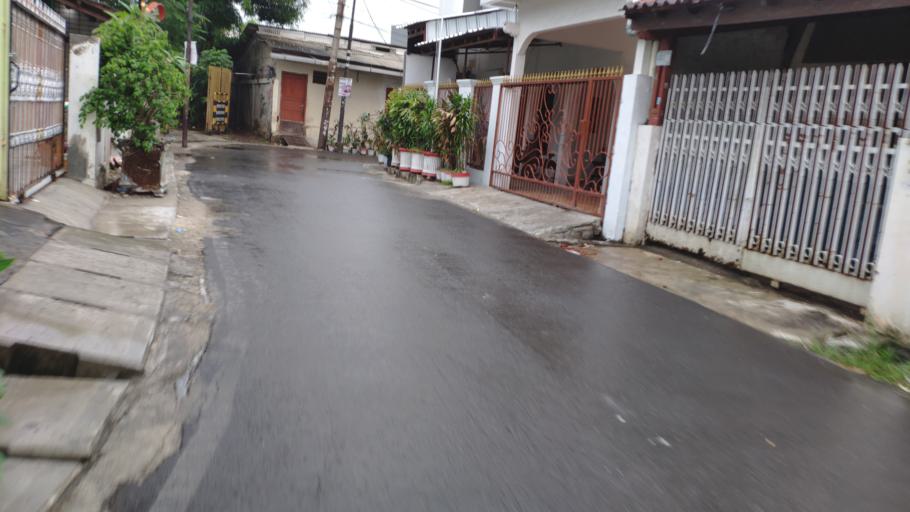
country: ID
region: Jakarta Raya
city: Jakarta
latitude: -6.2060
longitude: 106.8701
